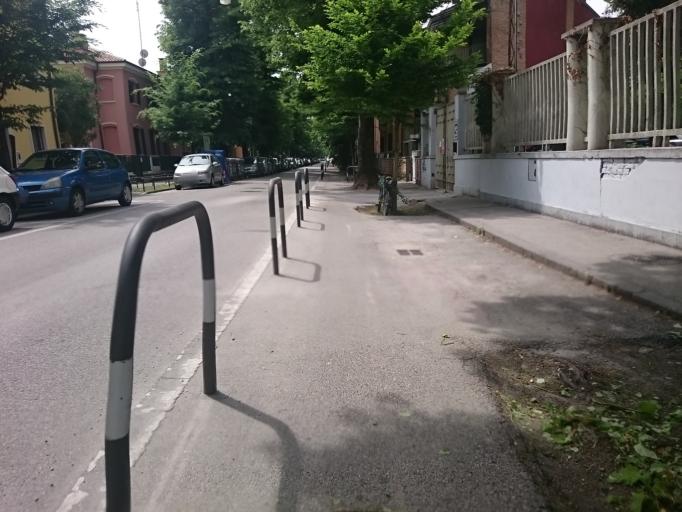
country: IT
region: Veneto
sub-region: Provincia di Padova
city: Padova
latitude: 45.3993
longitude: 11.8838
